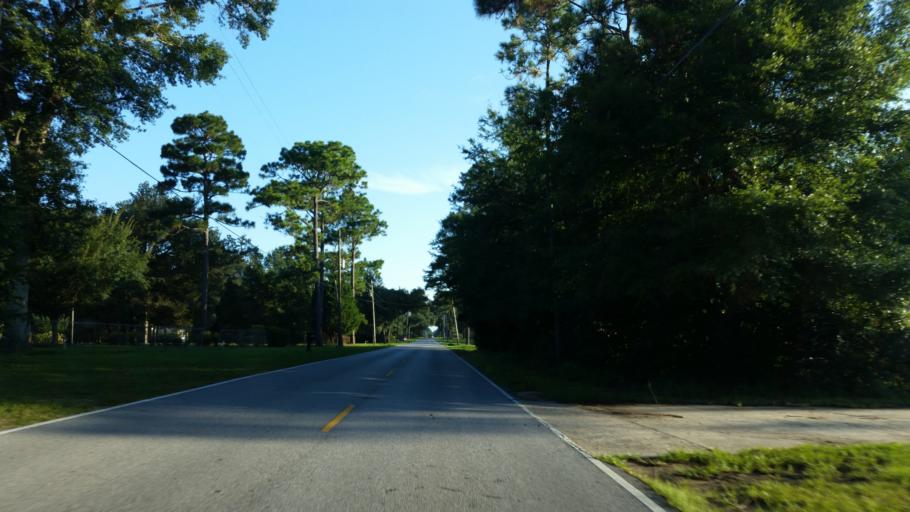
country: US
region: Florida
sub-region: Escambia County
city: Bellview
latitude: 30.5025
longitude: -87.3227
